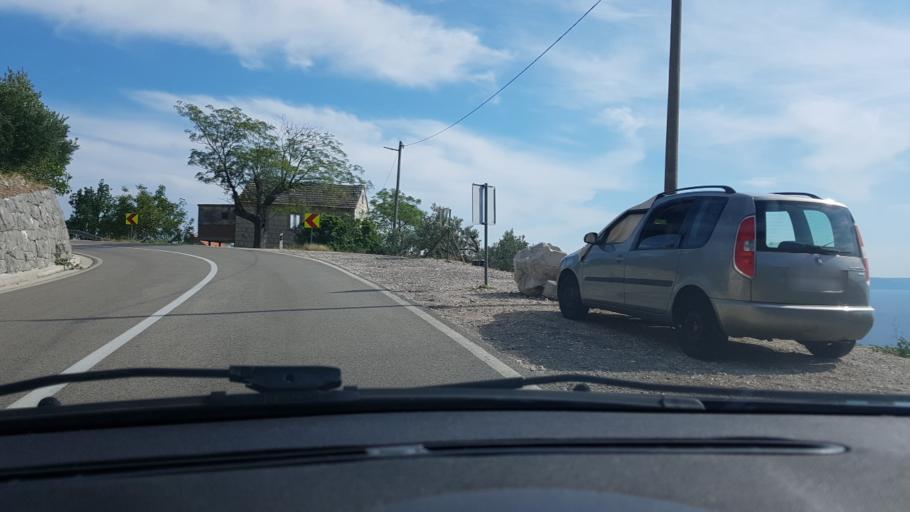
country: HR
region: Splitsko-Dalmatinska
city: Tucepi
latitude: 43.2771
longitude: 17.0631
